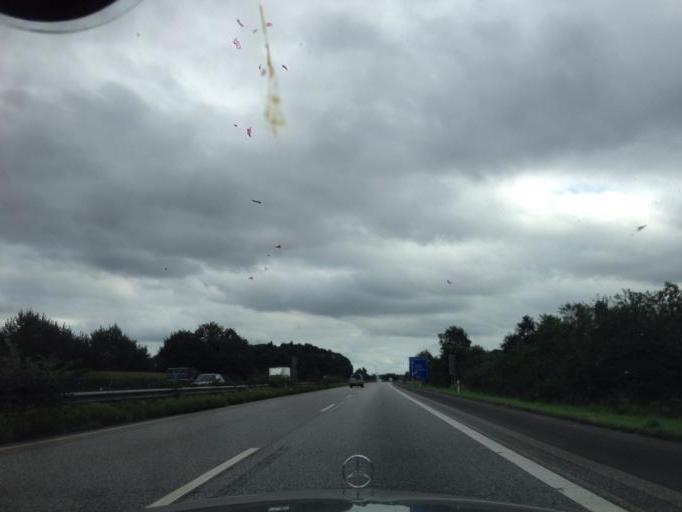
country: DE
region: Schleswig-Holstein
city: Gross Vollstedt
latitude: 54.2222
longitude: 9.8497
